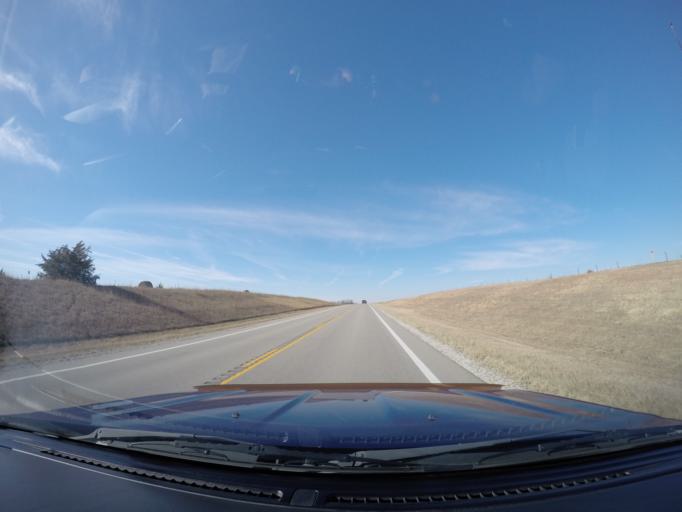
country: US
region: Kansas
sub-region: Clay County
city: Clay Center
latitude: 39.3787
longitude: -97.3214
